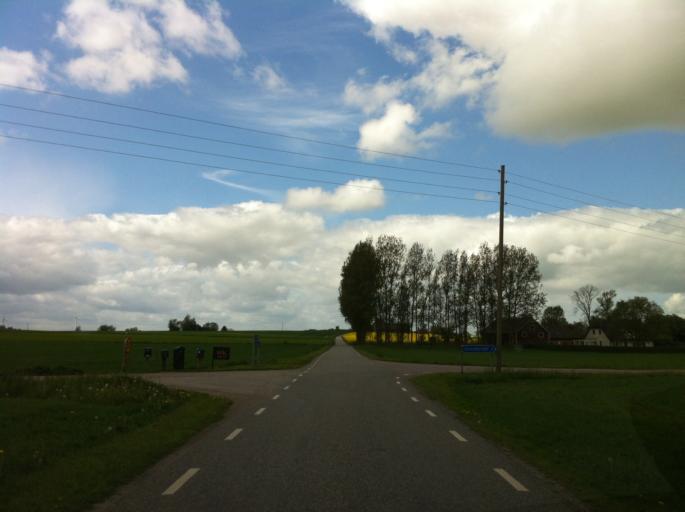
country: SE
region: Skane
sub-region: Svalovs Kommun
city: Teckomatorp
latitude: 55.8595
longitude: 13.0526
